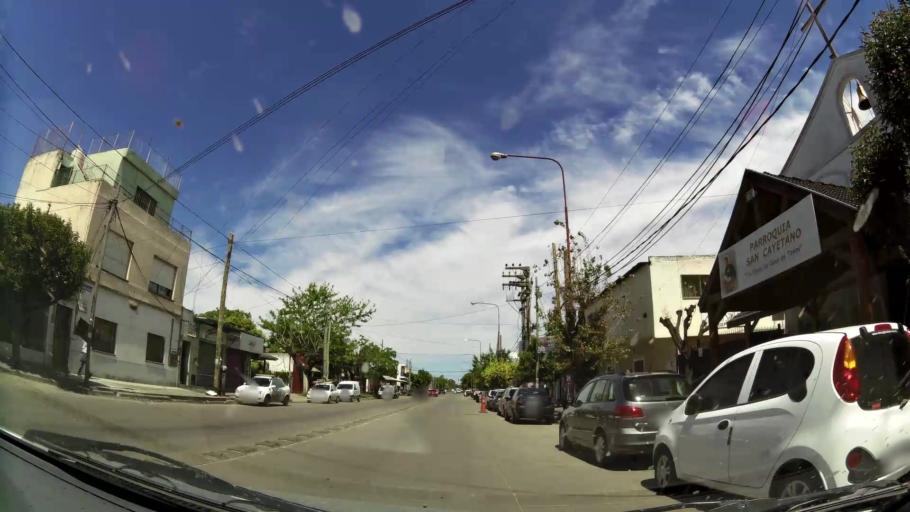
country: AR
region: Buenos Aires
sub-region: Partido de Quilmes
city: Quilmes
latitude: -34.7311
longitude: -58.3035
